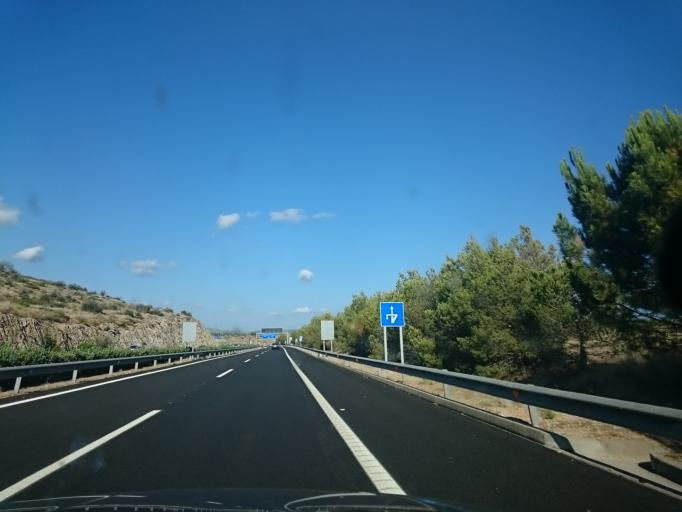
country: ES
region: Catalonia
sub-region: Provincia de Barcelona
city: Vilanova i la Geltru
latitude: 41.2494
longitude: 1.7034
